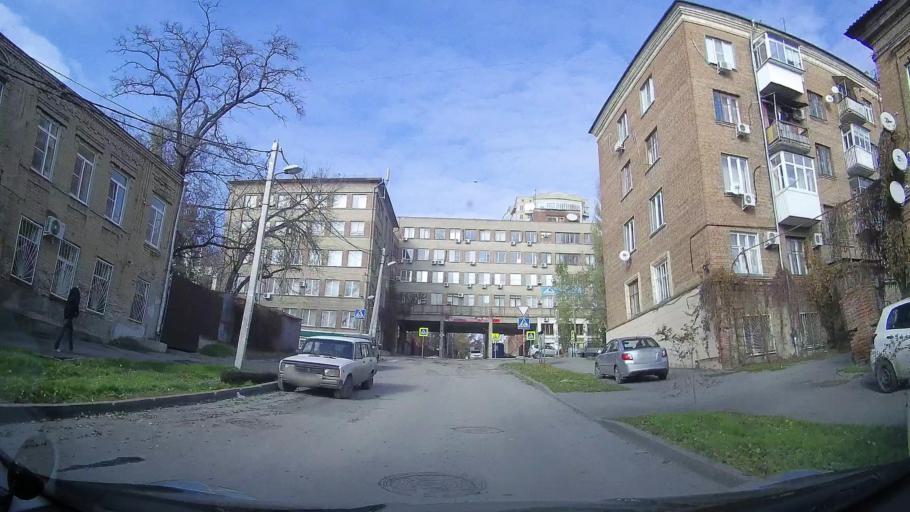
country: RU
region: Rostov
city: Rostov-na-Donu
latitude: 47.2217
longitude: 39.7360
